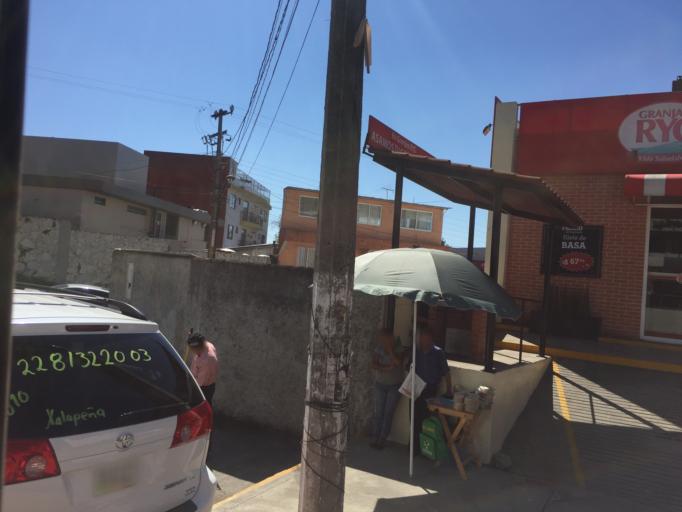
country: MX
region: Veracruz
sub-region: Xalapa
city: Xalapa de Enriquez
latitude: 19.5308
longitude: -96.9070
